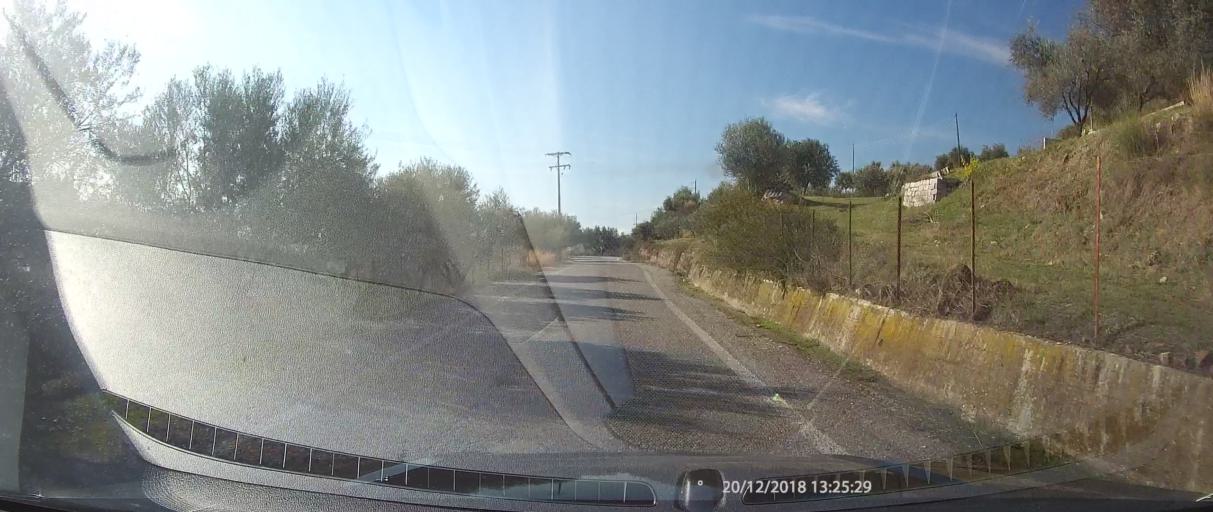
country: GR
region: West Greece
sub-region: Nomos Aitolias kai Akarnanias
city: Paravola
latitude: 38.6249
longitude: 21.5681
